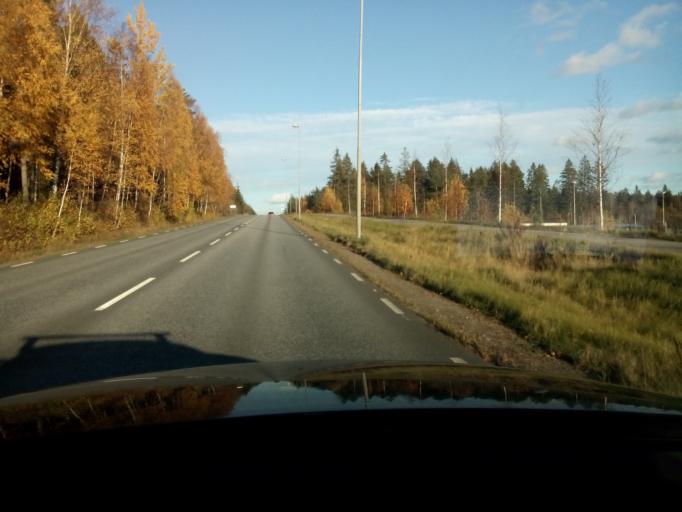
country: SE
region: Soedermanland
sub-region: Nykopings Kommun
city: Nykoping
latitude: 58.7157
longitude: 17.0215
